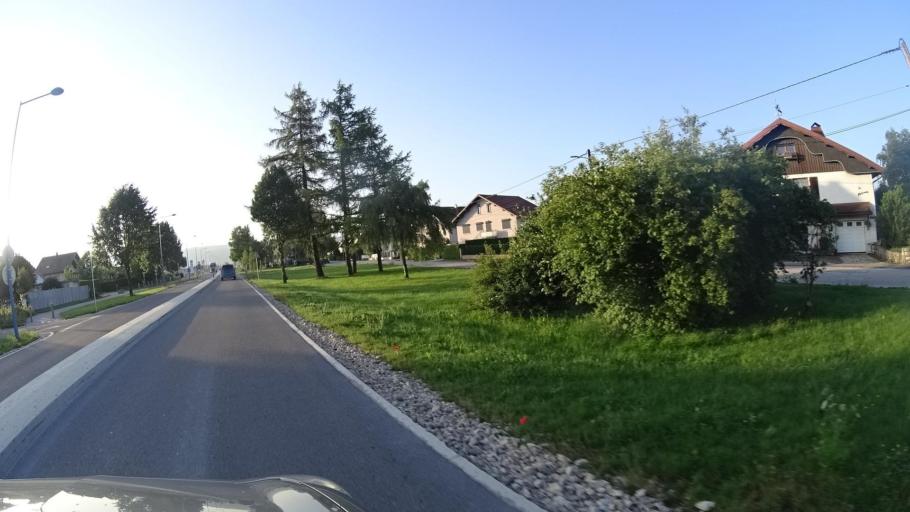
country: FR
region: Franche-Comte
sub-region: Departement du Doubs
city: Doubs
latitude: 46.9146
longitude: 6.3158
